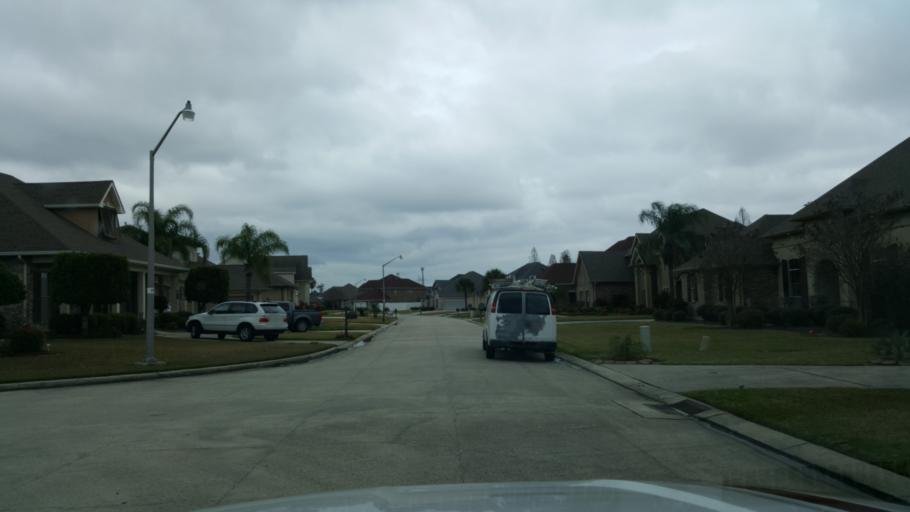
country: US
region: Louisiana
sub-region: Jefferson Parish
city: Woodmere
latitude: 29.8753
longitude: -90.0764
